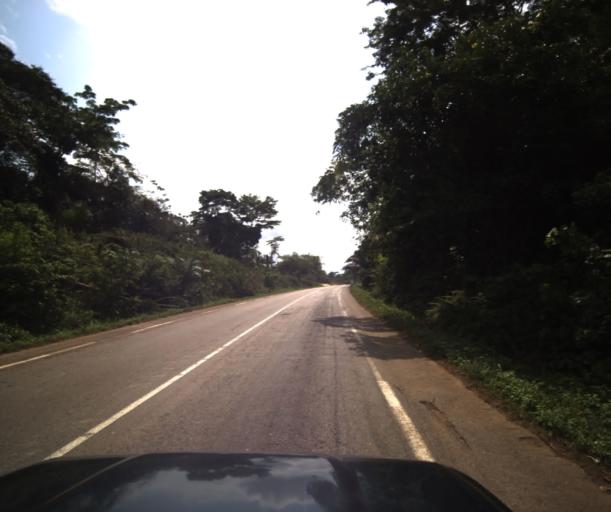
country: CM
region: Centre
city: Eseka
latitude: 3.8588
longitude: 10.5497
